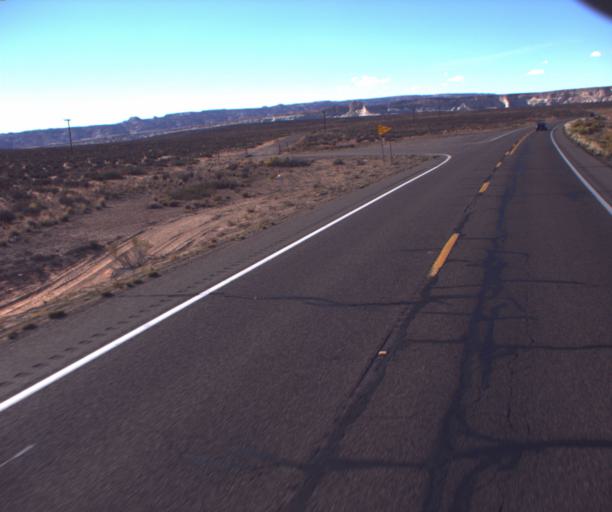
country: US
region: Arizona
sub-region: Coconino County
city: Page
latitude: 36.9838
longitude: -111.5512
